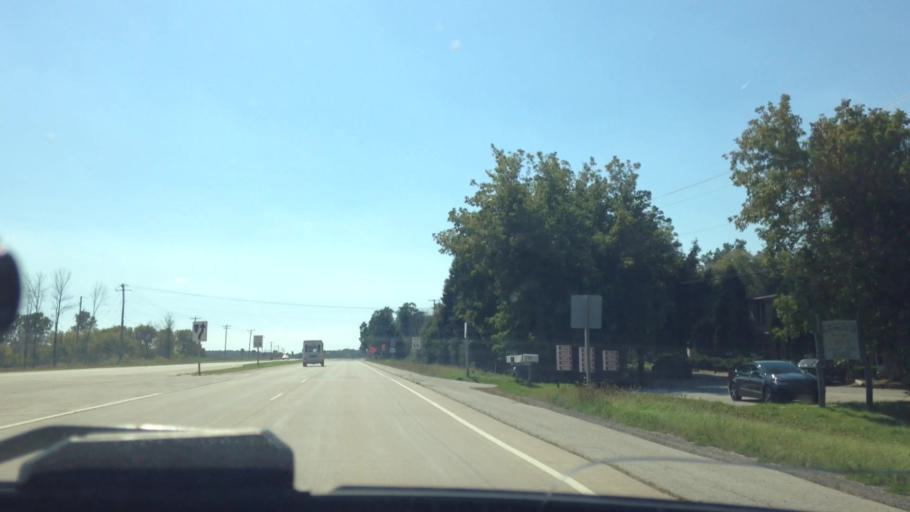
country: US
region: Wisconsin
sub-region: Ozaukee County
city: Saukville
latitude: 43.3473
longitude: -87.9186
